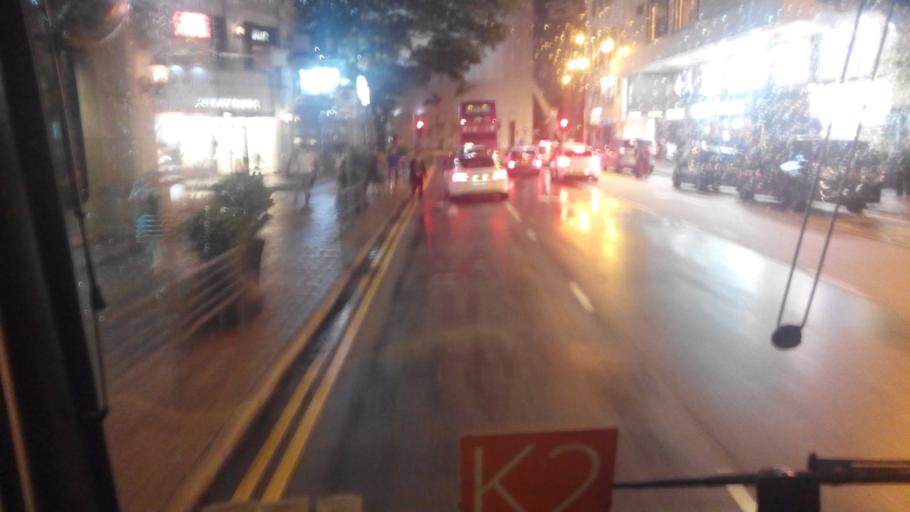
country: HK
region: Wanchai
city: Wan Chai
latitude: 22.2950
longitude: 114.1690
